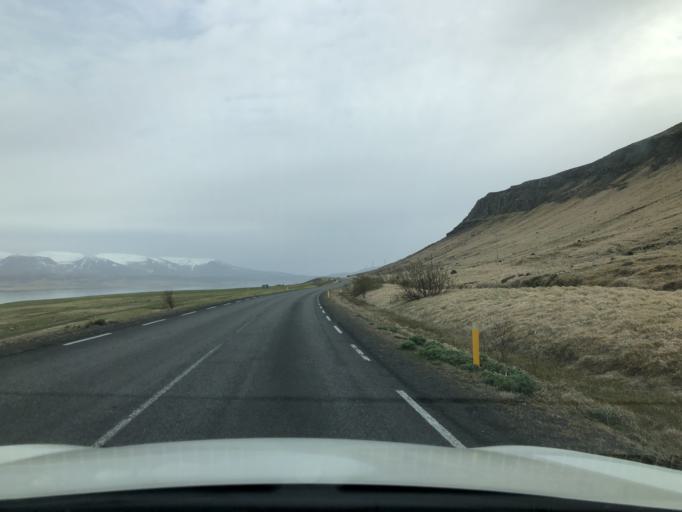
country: IS
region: Capital Region
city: Mosfellsbaer
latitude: 64.3149
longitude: -21.7674
